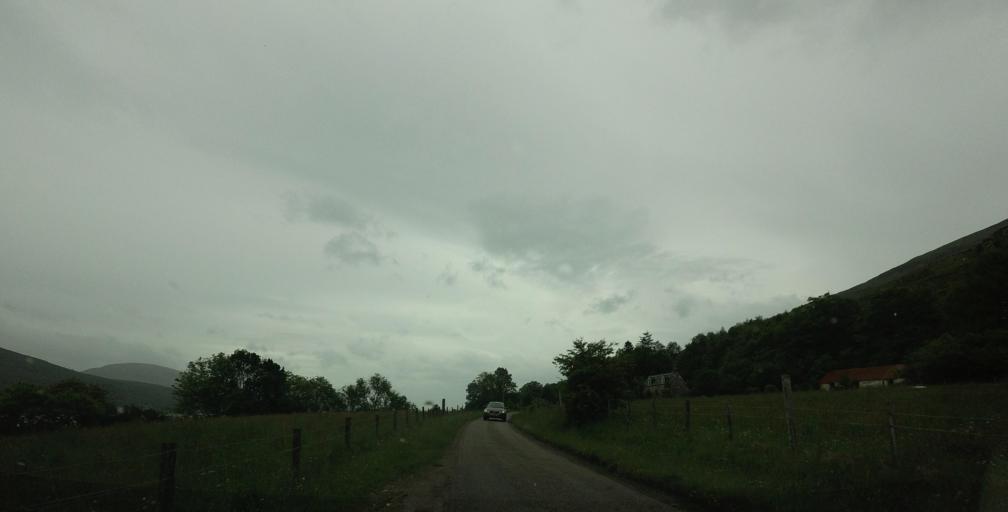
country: GB
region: Scotland
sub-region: Highland
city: Fort William
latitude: 56.8136
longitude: -5.1403
